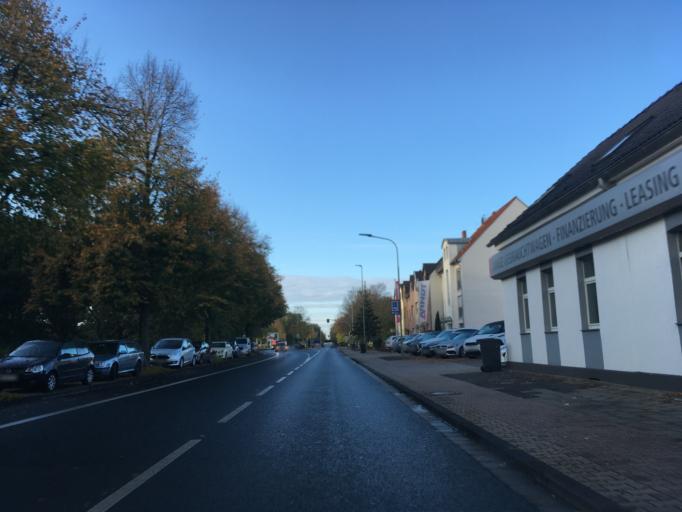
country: DE
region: North Rhine-Westphalia
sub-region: Regierungsbezirk Dusseldorf
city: Neuss
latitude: 51.1855
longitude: 6.6805
